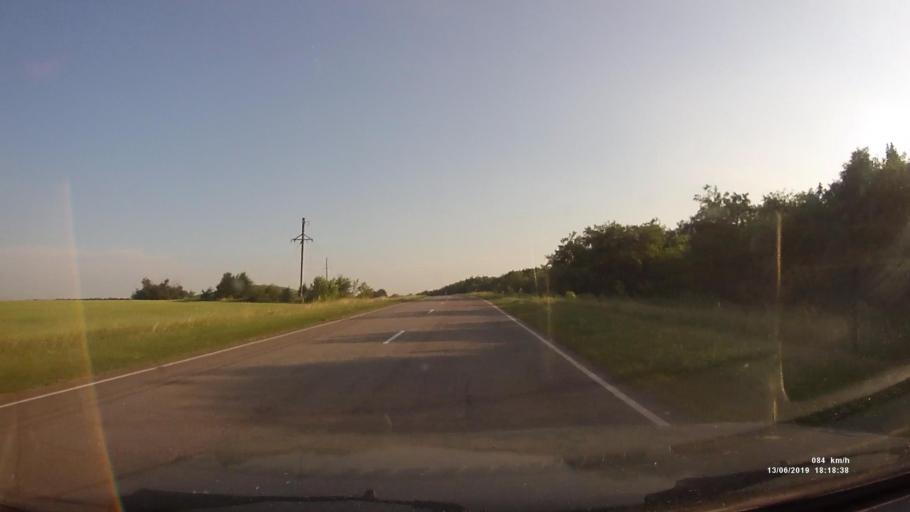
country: RU
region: Rostov
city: Kazanskaya
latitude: 49.9059
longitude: 41.3117
